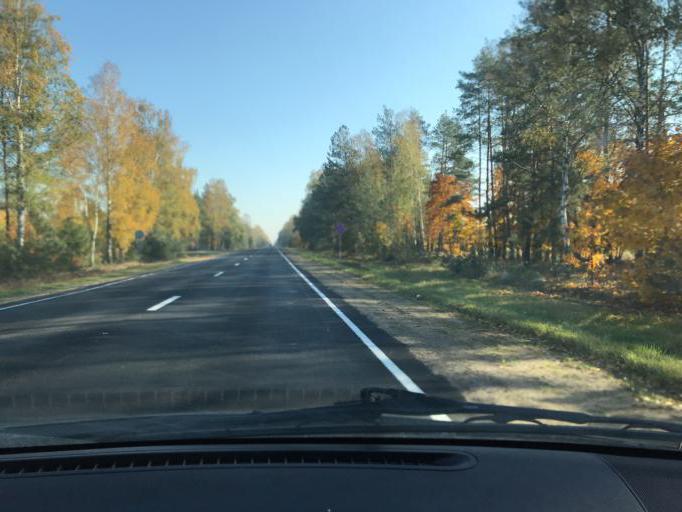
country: BY
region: Brest
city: Baranovichi
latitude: 52.9059
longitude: 25.9021
